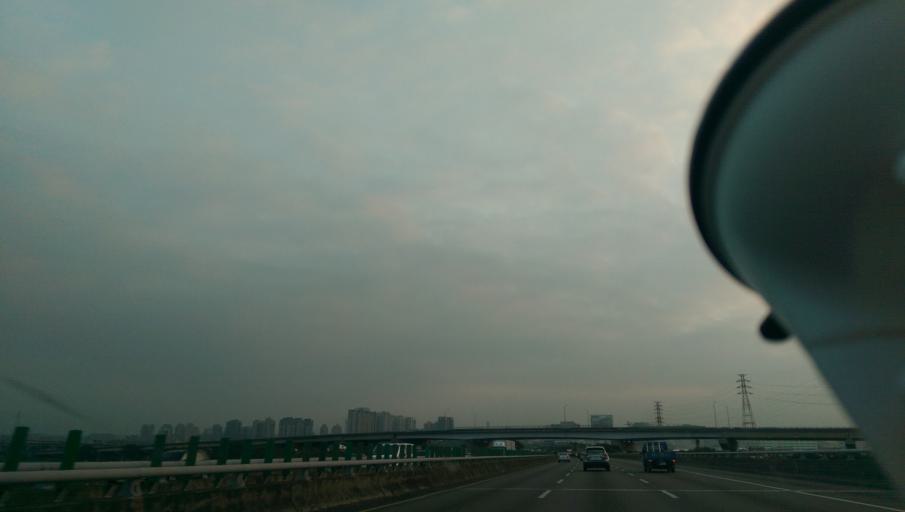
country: TW
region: Taiwan
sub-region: Hsinchu
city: Zhubei
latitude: 24.8133
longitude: 121.0117
